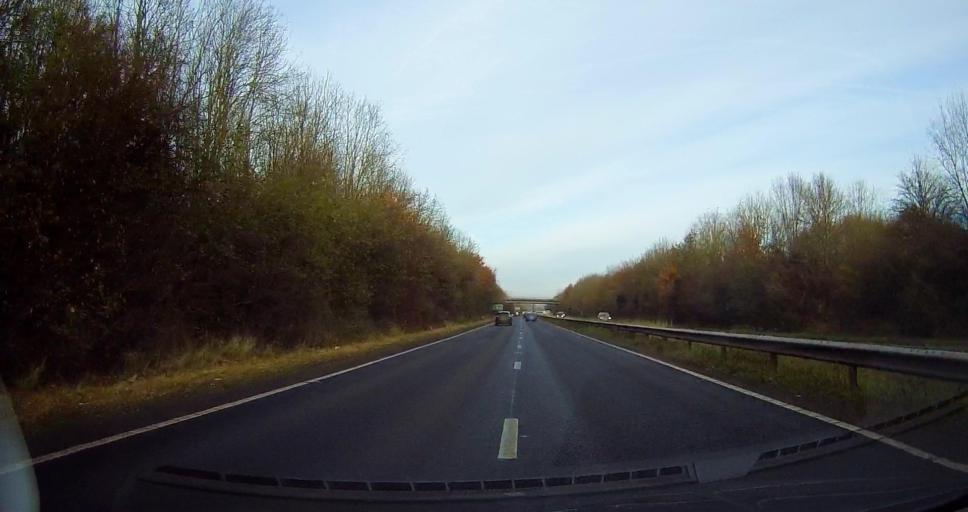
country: GB
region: England
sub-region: West Sussex
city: Hurstpierpoint
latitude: 50.9523
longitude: -0.1931
